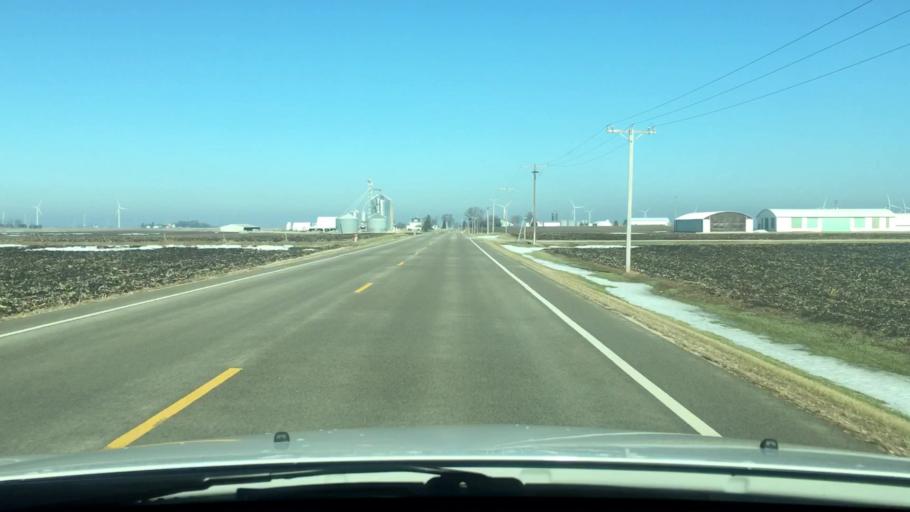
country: US
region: Illinois
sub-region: DeKalb County
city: Waterman
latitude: 41.7819
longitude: -88.8772
